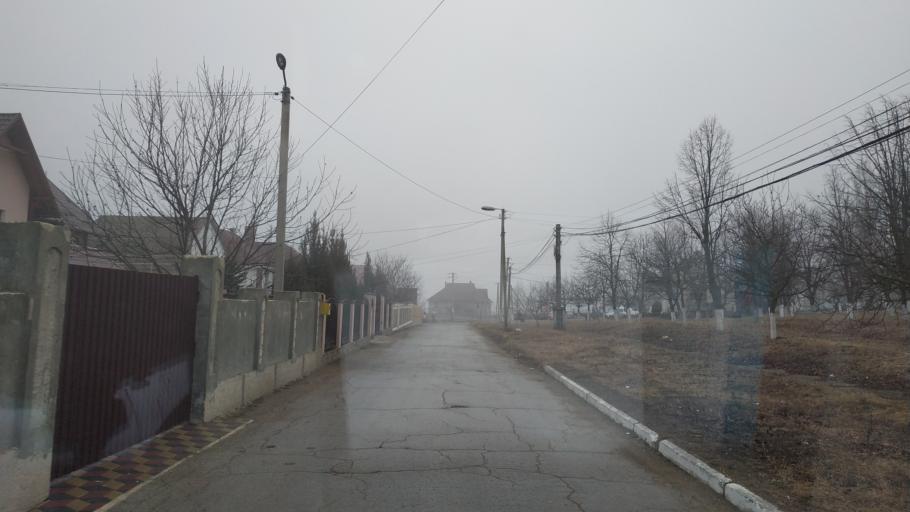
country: MD
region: Laloveni
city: Ialoveni
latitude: 46.9621
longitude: 28.7096
